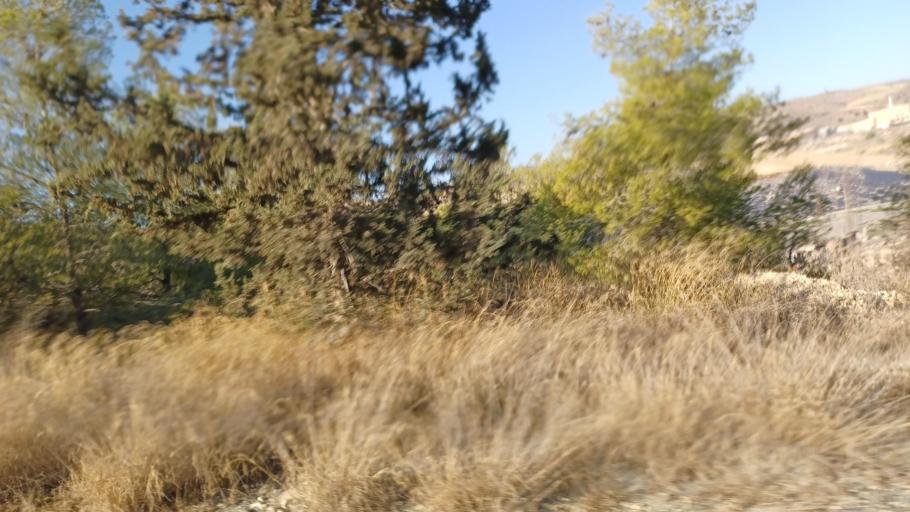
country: CY
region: Larnaka
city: Psevdas
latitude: 34.9623
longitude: 33.5135
